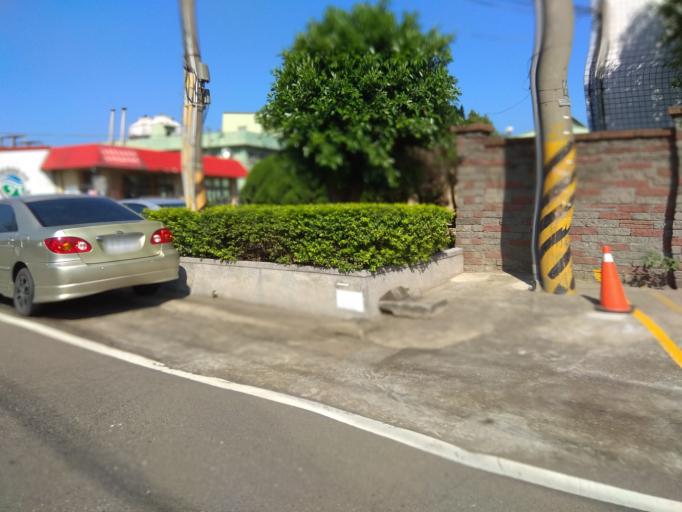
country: TW
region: Taiwan
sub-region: Hsinchu
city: Zhubei
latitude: 24.9816
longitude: 121.0366
